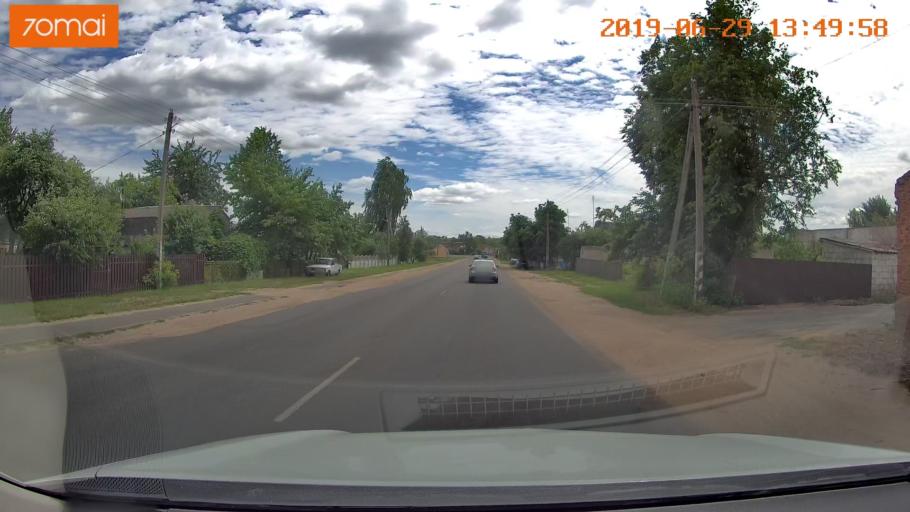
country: BY
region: Minsk
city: Slutsk
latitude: 53.0061
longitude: 27.5661
